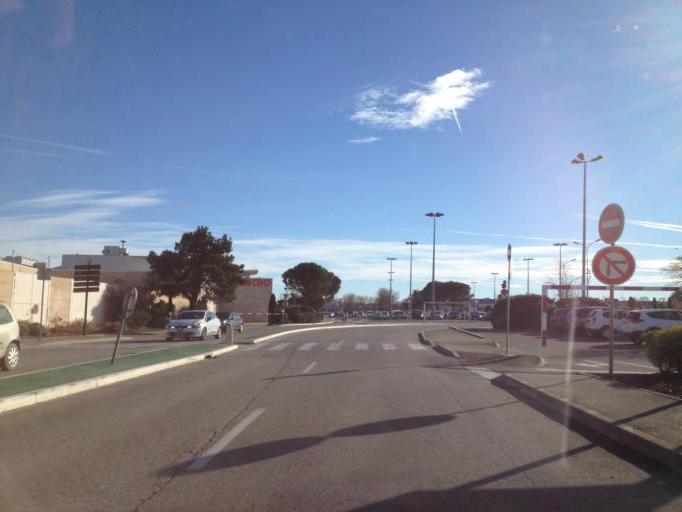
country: FR
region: Provence-Alpes-Cote d'Azur
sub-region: Departement du Vaucluse
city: Vedene
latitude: 43.9822
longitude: 4.8780
